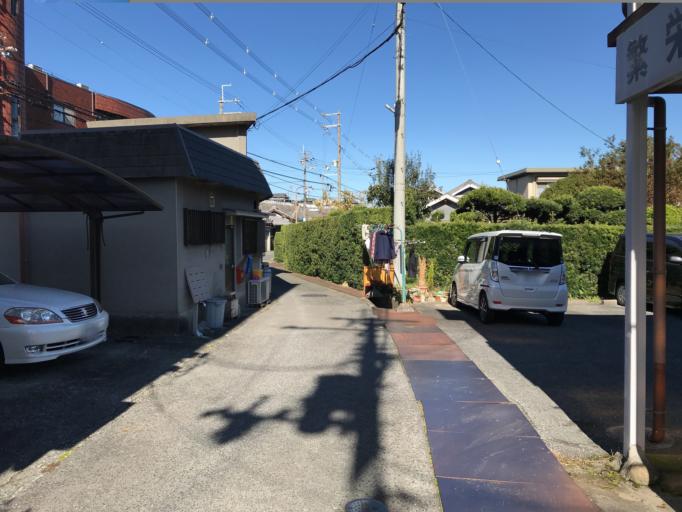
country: JP
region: Osaka
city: Tondabayashicho
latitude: 34.4586
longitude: 135.5768
